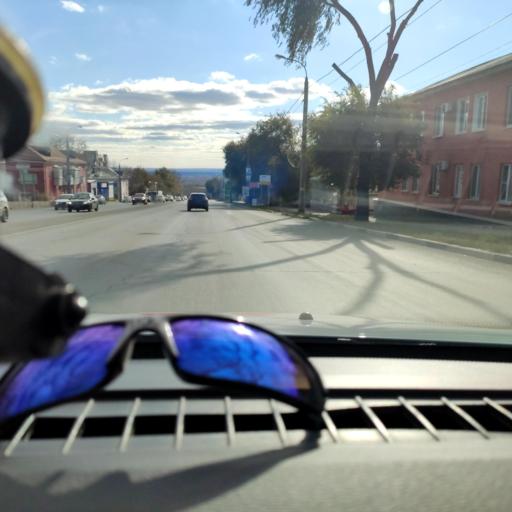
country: RU
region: Samara
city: Samara
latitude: 53.1837
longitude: 50.1915
